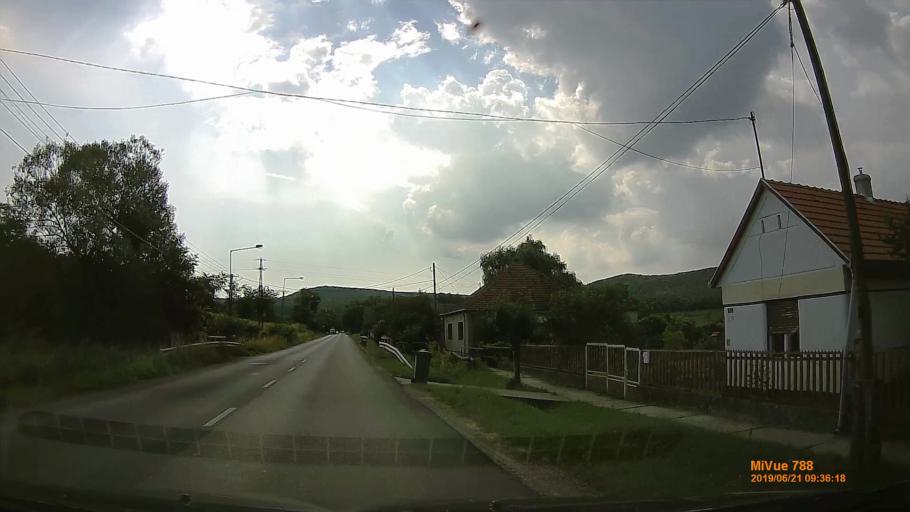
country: HU
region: Somogy
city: Taszar
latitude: 46.3175
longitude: 17.9018
